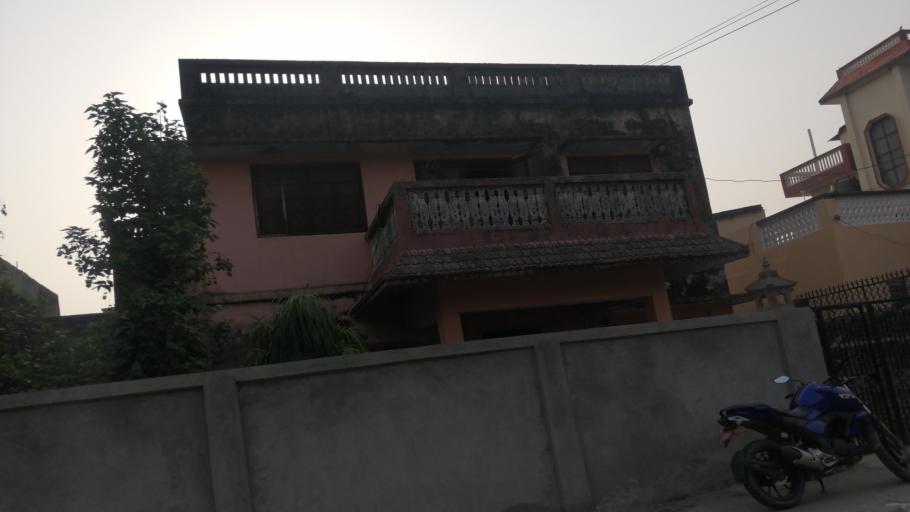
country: NP
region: Western Region
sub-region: Lumbini Zone
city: Bhairahawa
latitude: 27.4994
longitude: 83.4504
